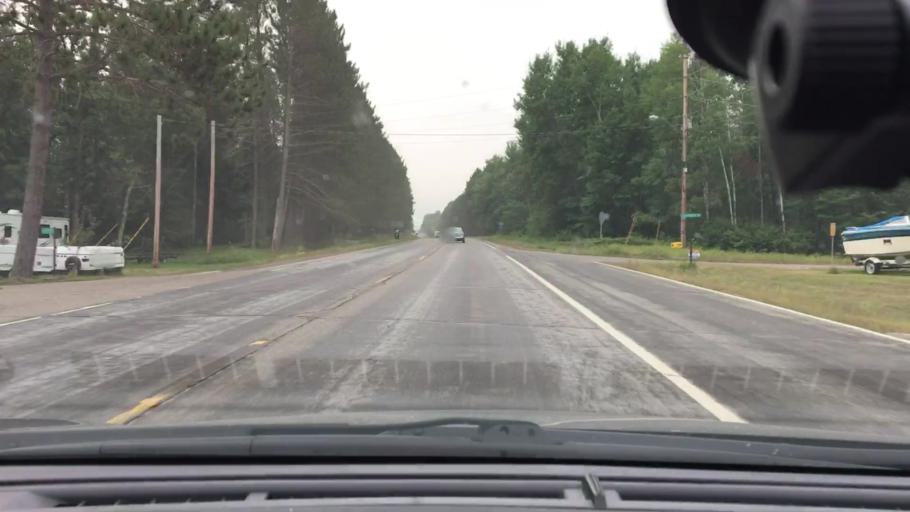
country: US
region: Minnesota
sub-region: Crow Wing County
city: Cross Lake
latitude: 46.7882
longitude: -93.9662
